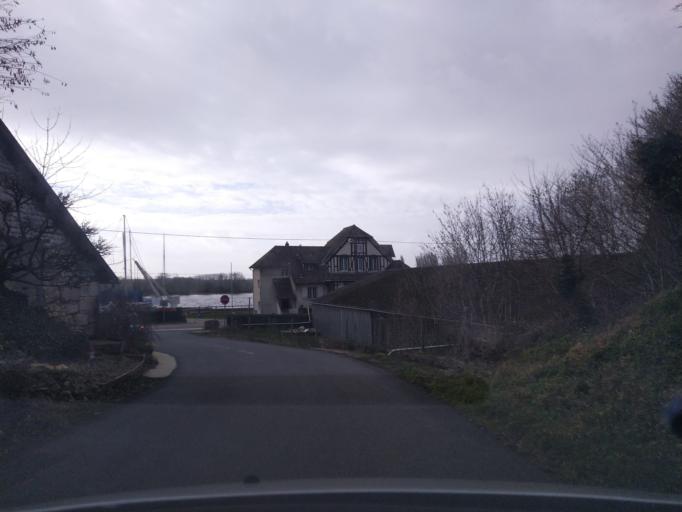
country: FR
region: Haute-Normandie
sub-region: Departement de la Seine-Maritime
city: Duclair
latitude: 49.4868
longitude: 0.8983
